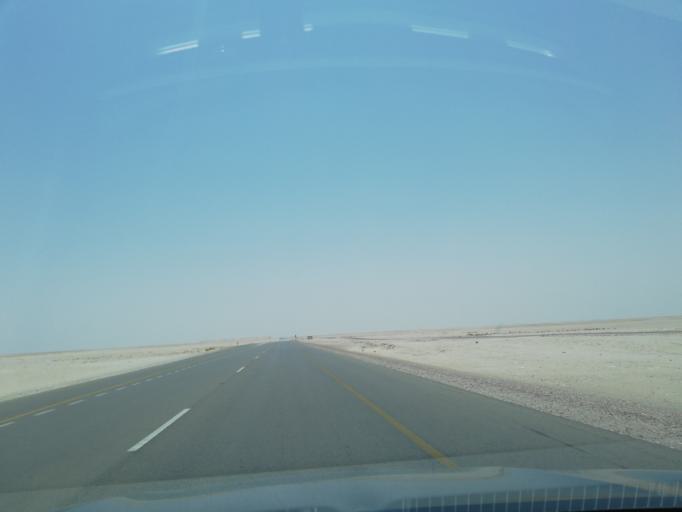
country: OM
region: Al Wusta
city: Hayma'
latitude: 19.8038
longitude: 56.1330
